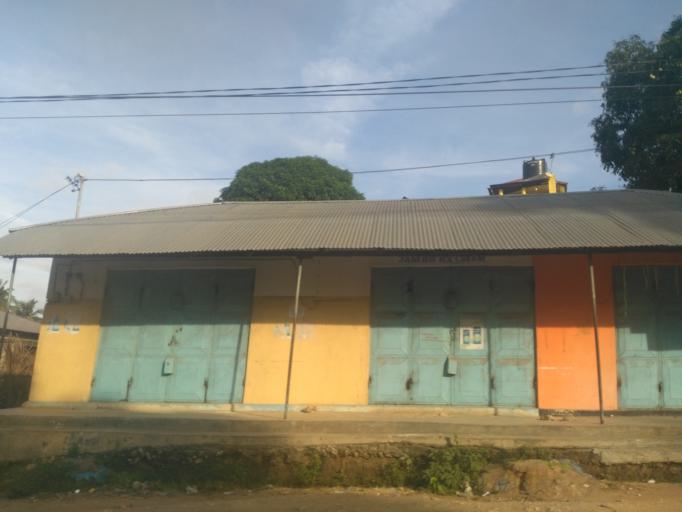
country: TZ
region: Zanzibar Urban/West
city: Zanzibar
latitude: -6.1480
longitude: 39.2373
